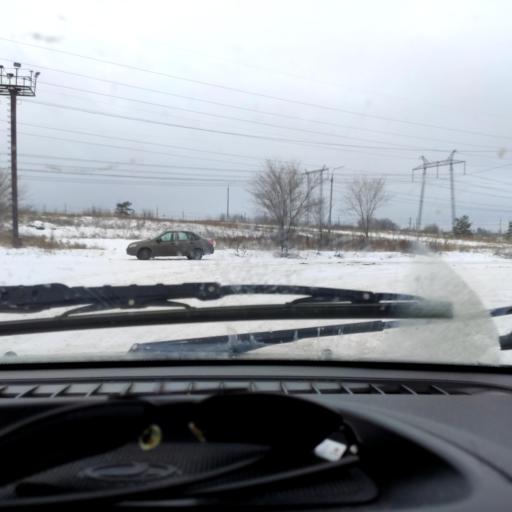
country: RU
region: Samara
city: Zhigulevsk
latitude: 53.5155
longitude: 49.5274
